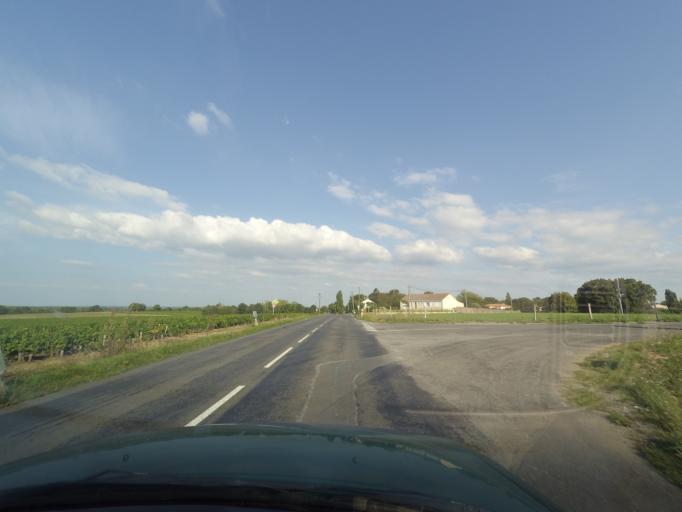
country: FR
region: Pays de la Loire
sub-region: Departement de la Loire-Atlantique
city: Saint-Philbert-de-Grand-Lieu
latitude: 47.0352
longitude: -1.6844
